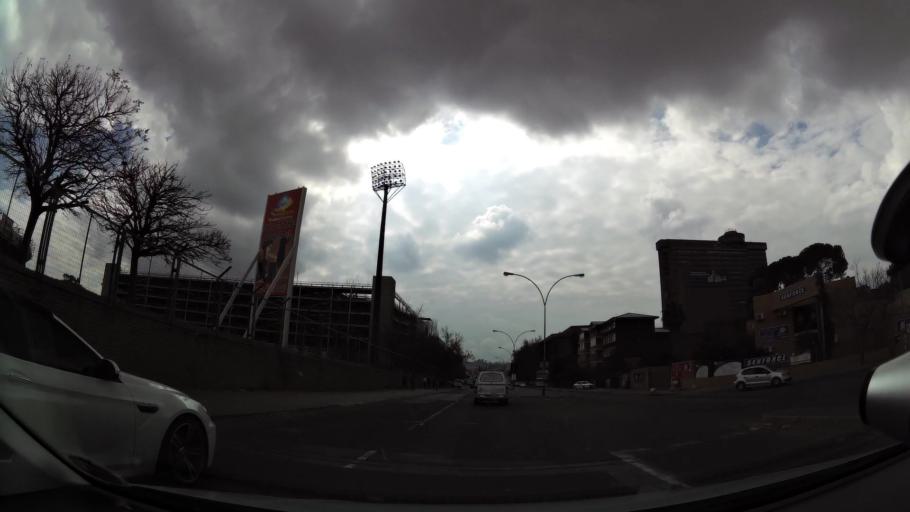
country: ZA
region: Orange Free State
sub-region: Mangaung Metropolitan Municipality
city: Bloemfontein
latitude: -29.1176
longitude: 26.2110
